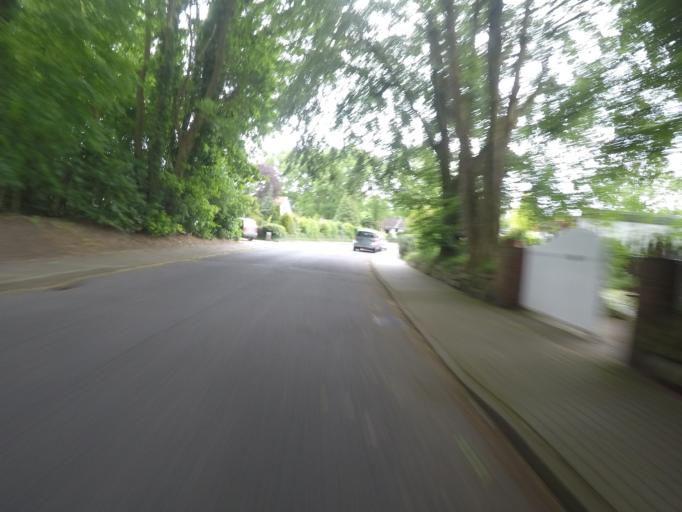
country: DE
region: Schleswig-Holstein
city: Quickborn
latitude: 53.7238
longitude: 9.9120
